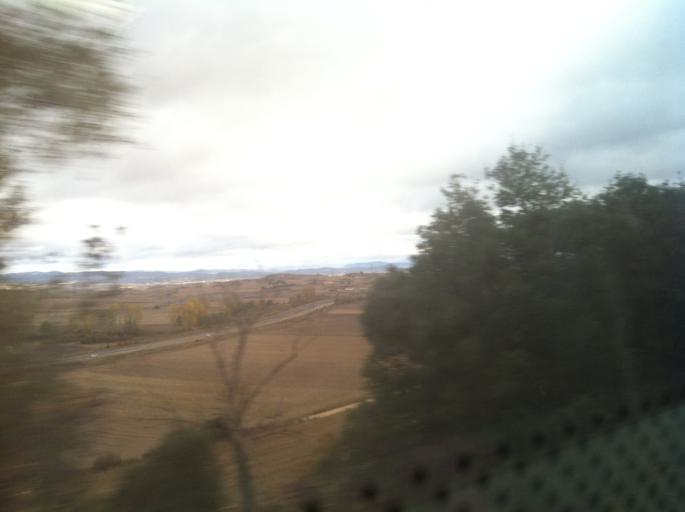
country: ES
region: Castille and Leon
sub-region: Provincia de Burgos
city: Ameyugo
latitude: 42.6528
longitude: -3.0568
